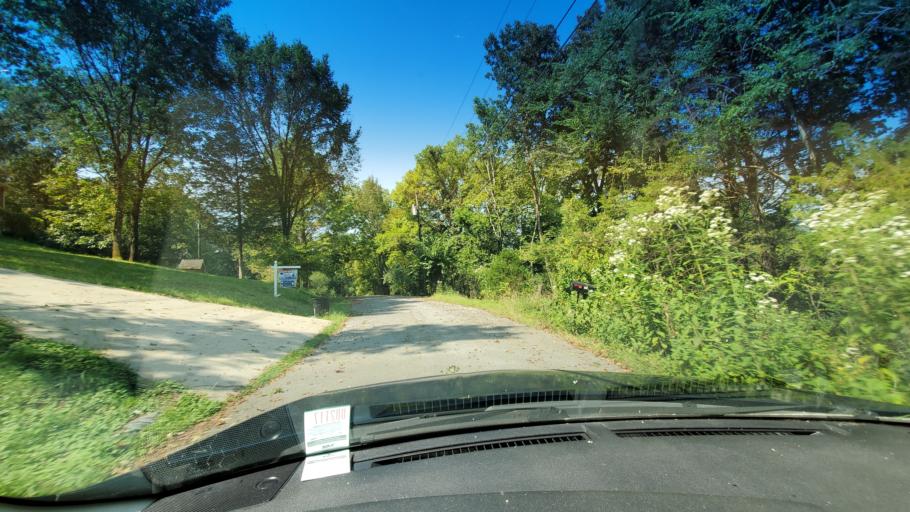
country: US
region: Tennessee
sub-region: Smith County
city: Carthage
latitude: 36.2508
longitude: -85.9623
